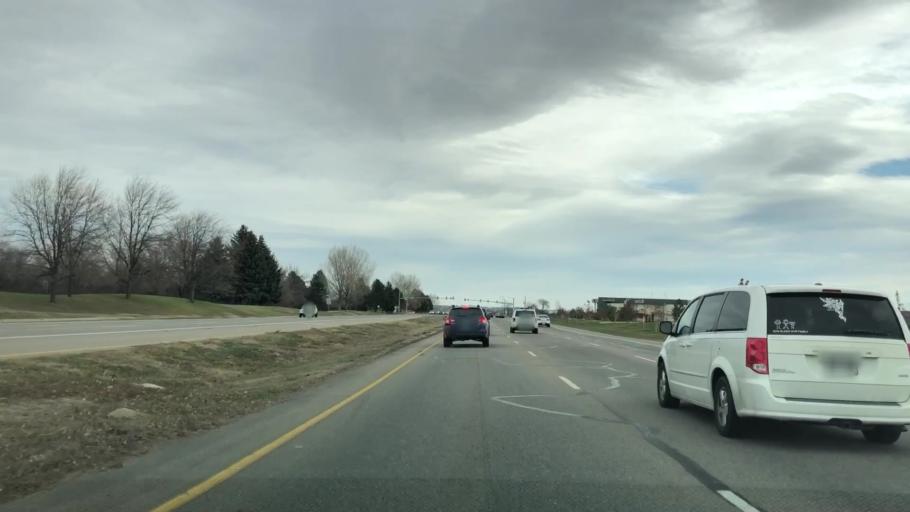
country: US
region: Colorado
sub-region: Larimer County
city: Fort Collins
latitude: 40.5233
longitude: -105.0151
